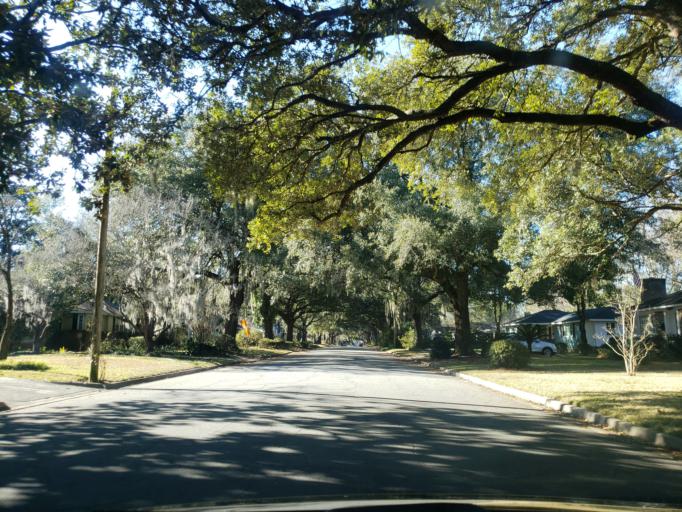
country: US
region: Georgia
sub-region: Chatham County
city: Thunderbolt
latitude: 32.0246
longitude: -81.0991
